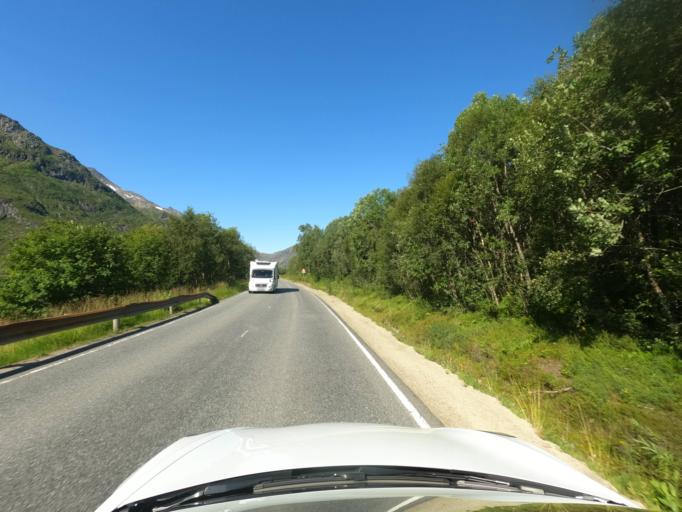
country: NO
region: Nordland
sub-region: Lodingen
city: Lodingen
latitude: 68.5603
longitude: 15.7625
